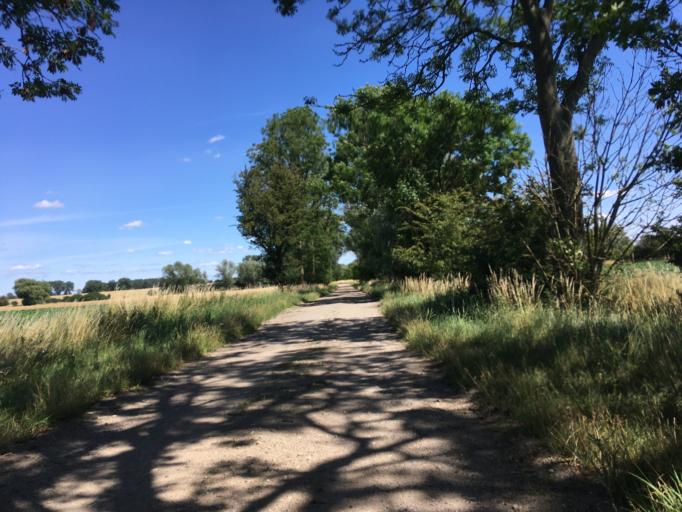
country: DE
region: Brandenburg
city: Grunow
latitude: 53.3370
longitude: 14.0087
